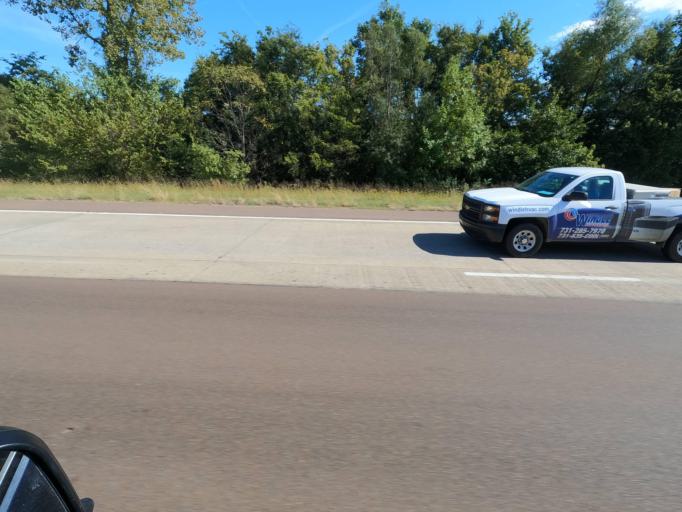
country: US
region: Tennessee
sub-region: Dyer County
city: Dyersburg
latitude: 36.0306
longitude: -89.3400
